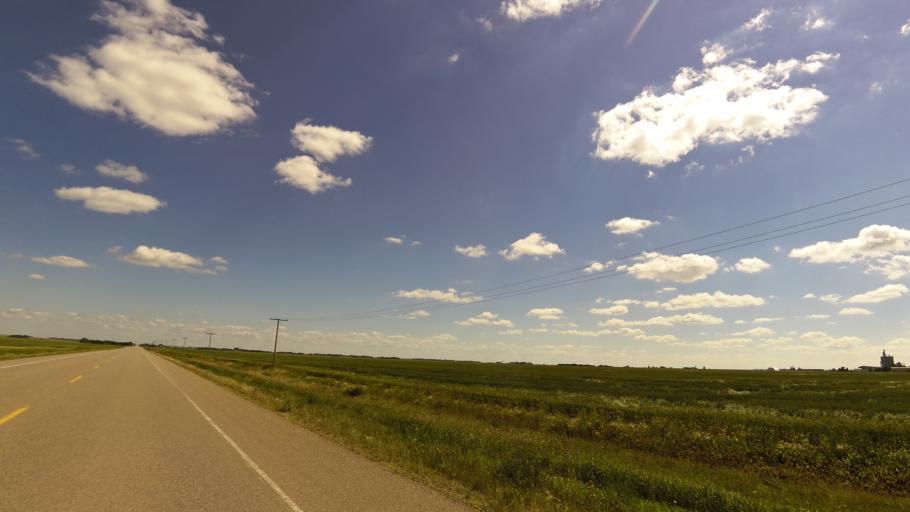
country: CA
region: Saskatchewan
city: Unity
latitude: 52.7548
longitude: -109.0149
